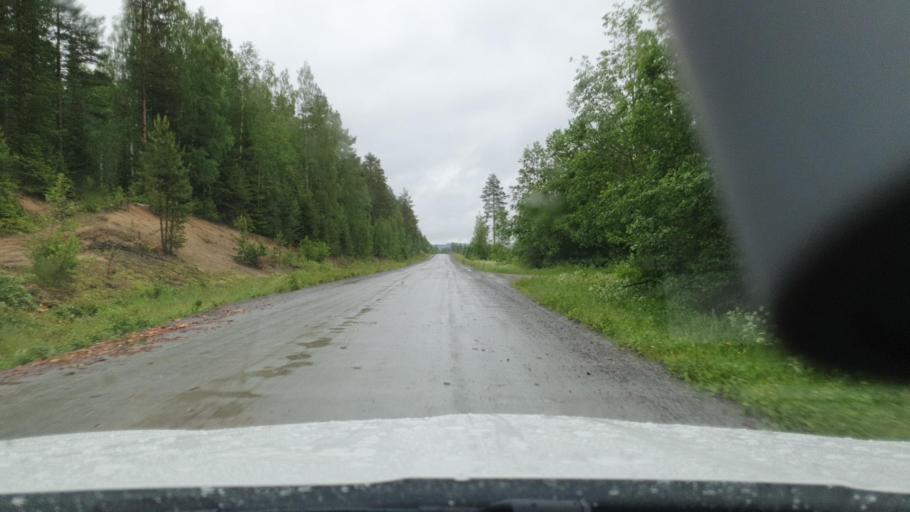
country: SE
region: Vaesterbotten
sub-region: Skelleftea Kommun
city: Burtraesk
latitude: 64.3754
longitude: 20.3599
